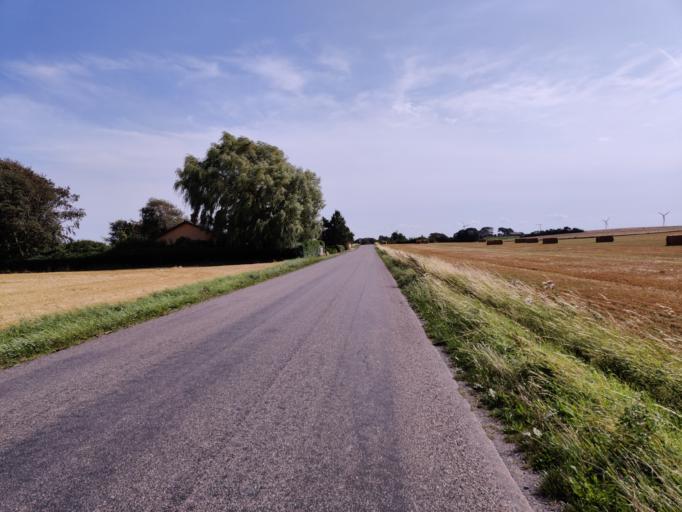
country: DK
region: Zealand
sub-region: Guldborgsund Kommune
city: Nykobing Falster
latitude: 54.6189
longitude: 11.9142
